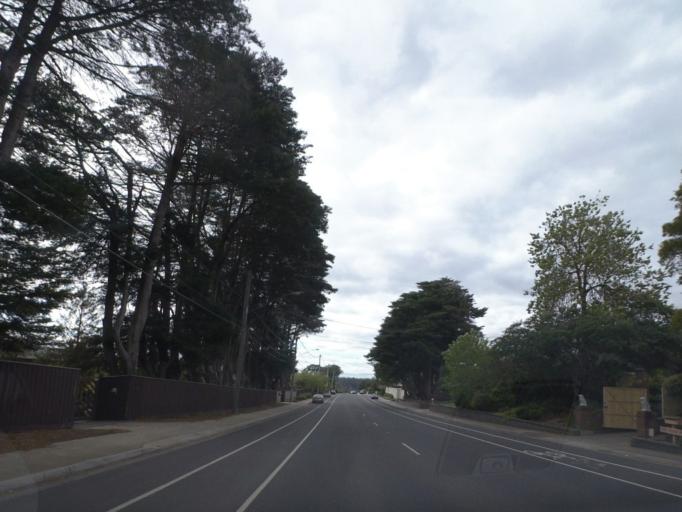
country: AU
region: Victoria
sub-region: Manningham
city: Templestowe Lower
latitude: -37.7621
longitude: 145.1190
